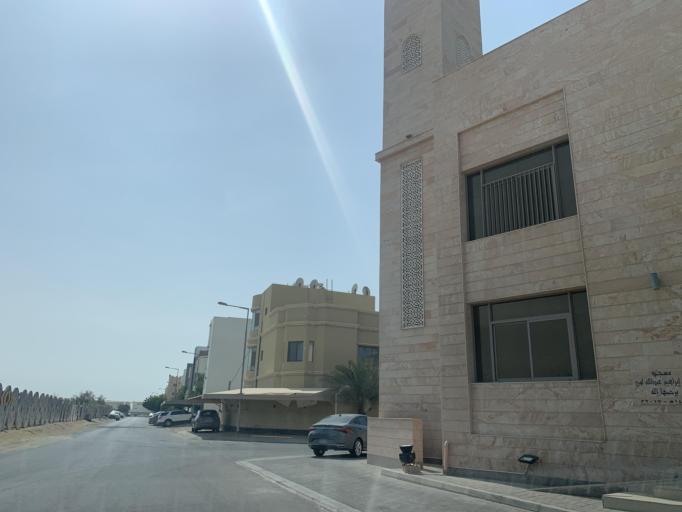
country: BH
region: Muharraq
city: Al Hadd
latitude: 26.2634
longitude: 50.6589
